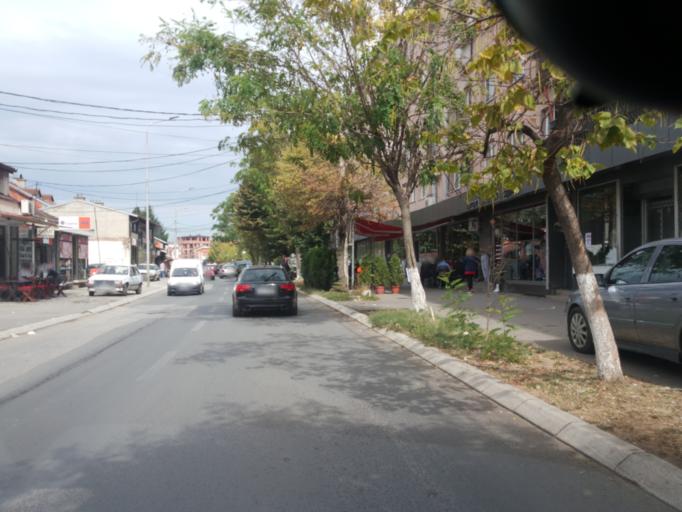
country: XK
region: Gjakova
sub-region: Komuna e Gjakoves
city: Gjakove
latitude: 42.3871
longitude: 20.4277
